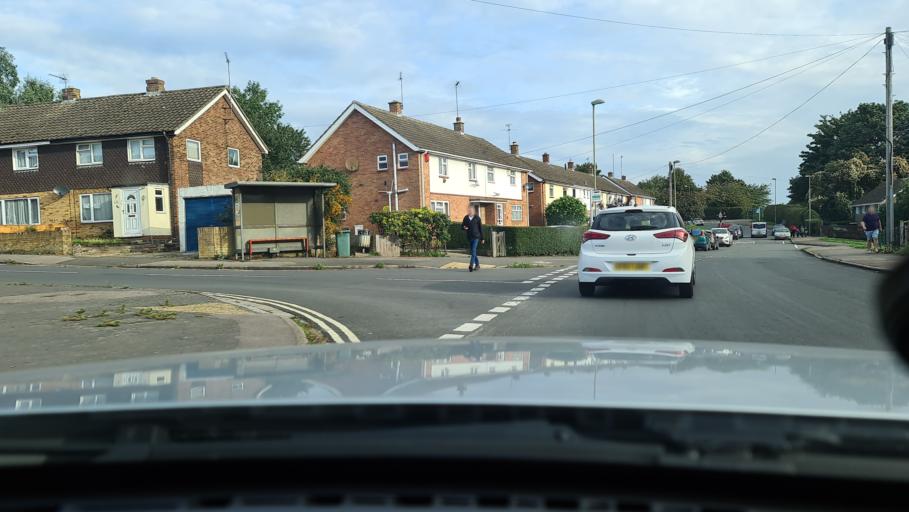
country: GB
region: England
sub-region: Oxfordshire
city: Banbury
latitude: 52.0655
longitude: -1.3653
